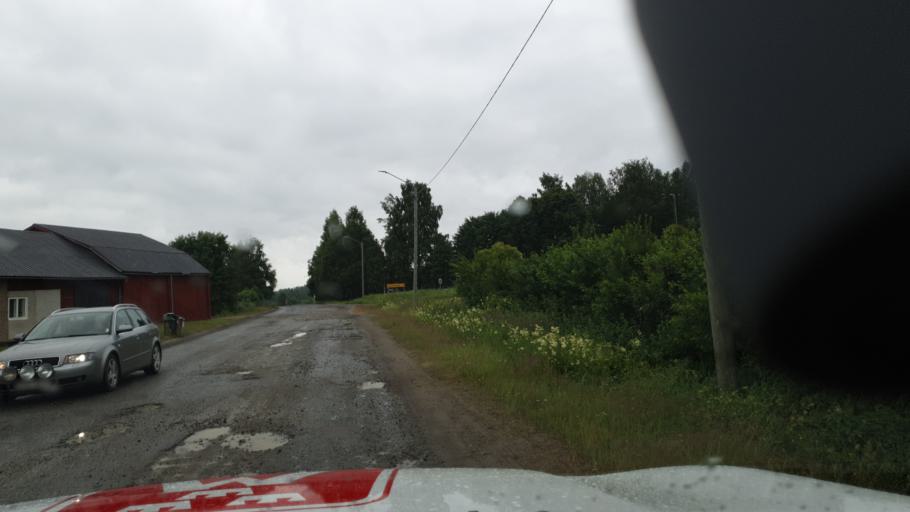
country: SE
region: Vaesterbotten
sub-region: Vannas Kommun
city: Vaennaes
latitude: 63.7828
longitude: 19.8408
